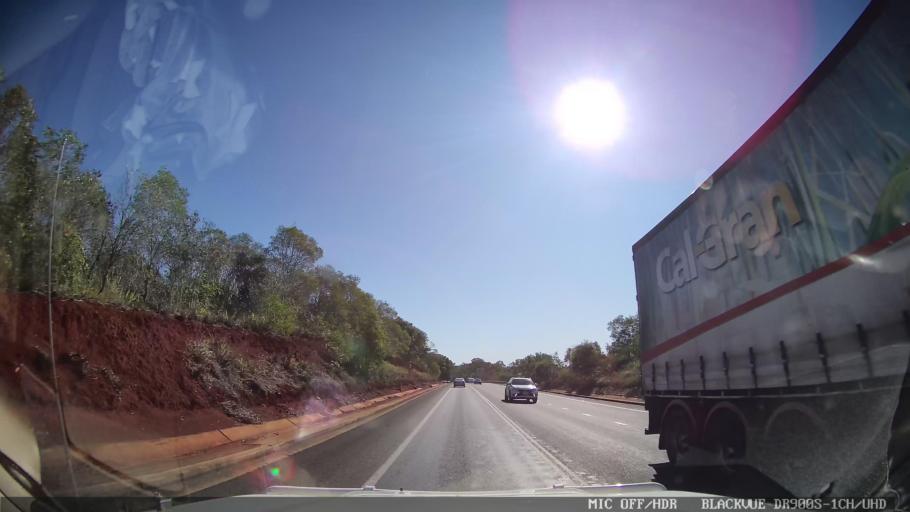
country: AU
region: Queensland
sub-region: Bundaberg
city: Childers
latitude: -25.2360
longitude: 152.2517
